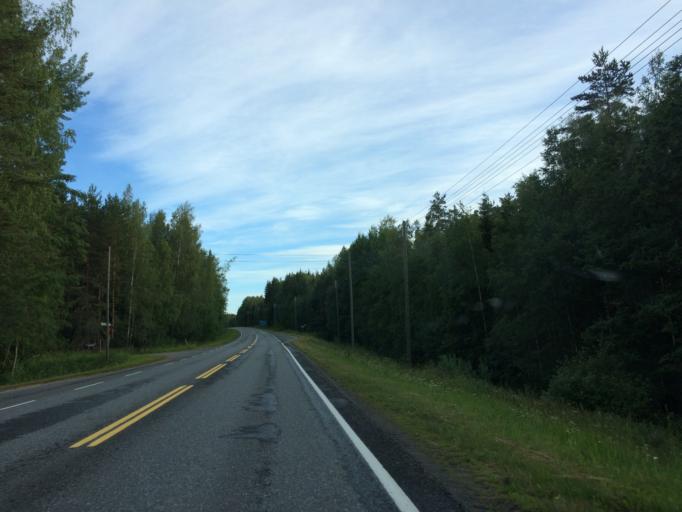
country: FI
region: Haeme
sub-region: Haemeenlinna
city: Janakkala
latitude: 60.9089
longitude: 24.5532
